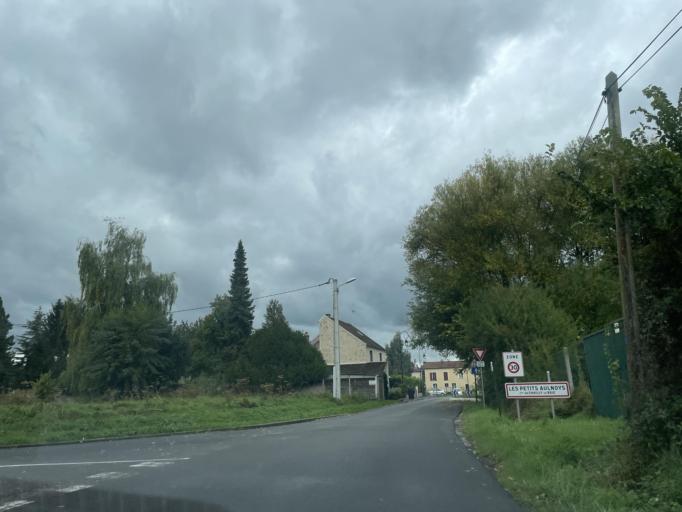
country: FR
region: Ile-de-France
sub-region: Departement de Seine-et-Marne
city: Chailly-en-Brie
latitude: 48.8090
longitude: 3.1140
